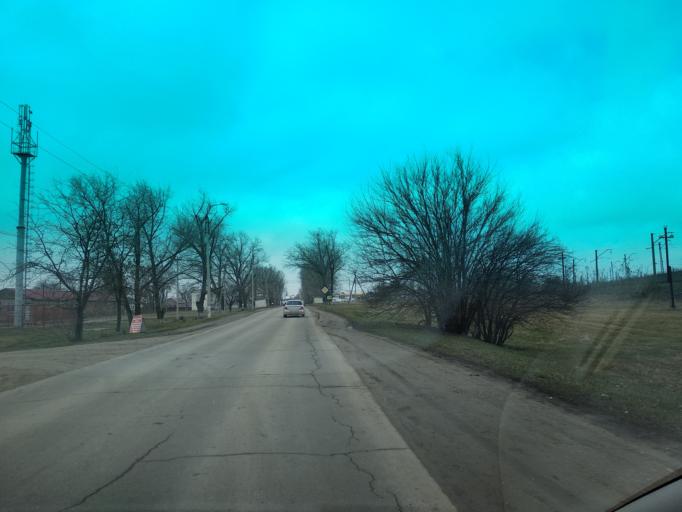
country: RU
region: Krasnodarskiy
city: Parkovyy
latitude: 45.8368
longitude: 40.1285
